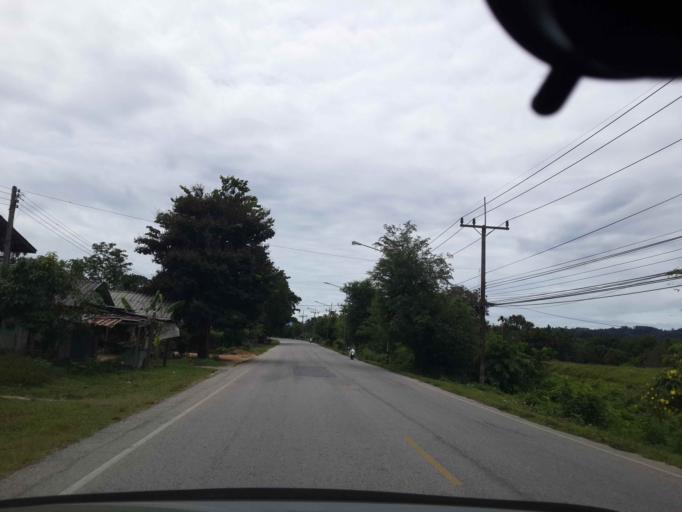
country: TH
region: Narathiwat
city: Yi-ngo
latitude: 6.3469
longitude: 101.6230
